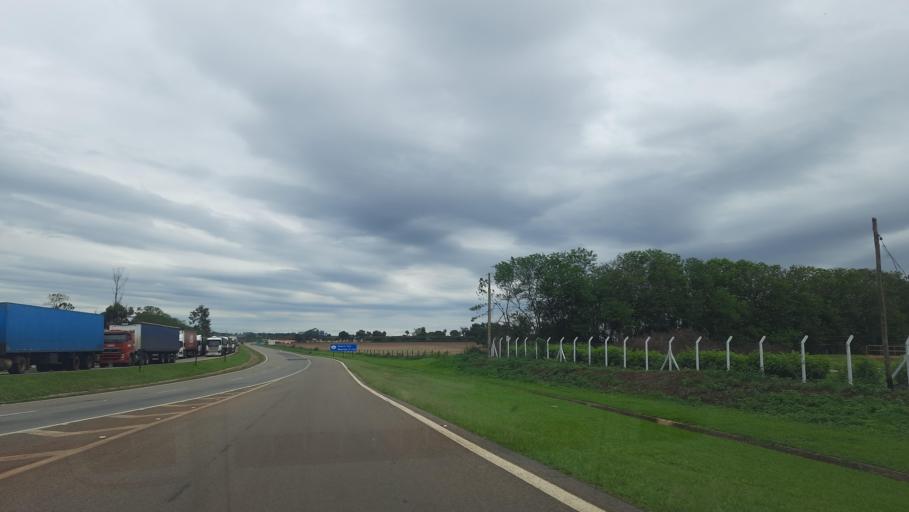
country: BR
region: Sao Paulo
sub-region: Casa Branca
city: Casa Branca
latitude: -21.7882
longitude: -47.0643
